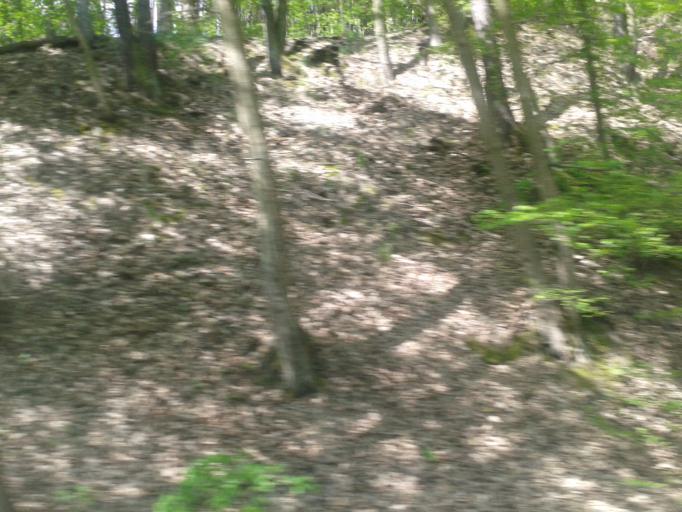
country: CZ
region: Central Bohemia
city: Lochovice
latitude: 49.8315
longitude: 13.9653
